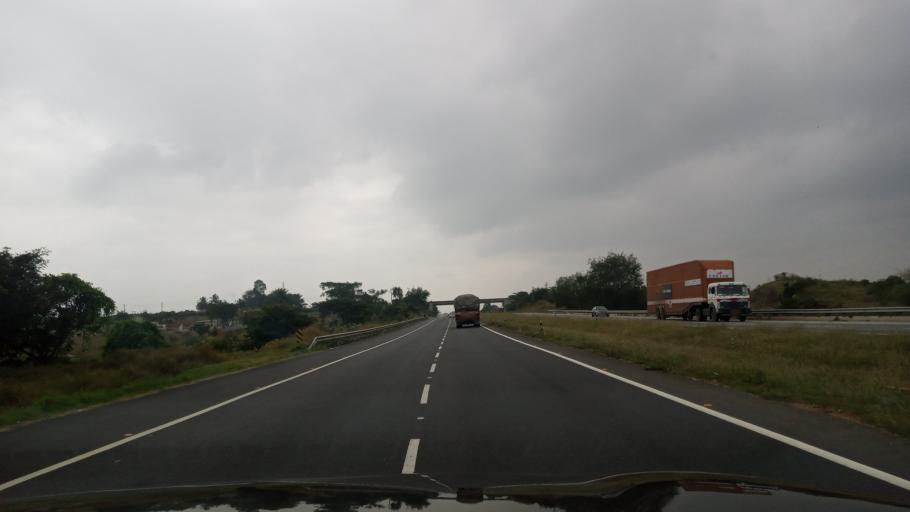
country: IN
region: Karnataka
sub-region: Bangalore Urban
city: Bangalore
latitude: 12.9744
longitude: 77.4714
